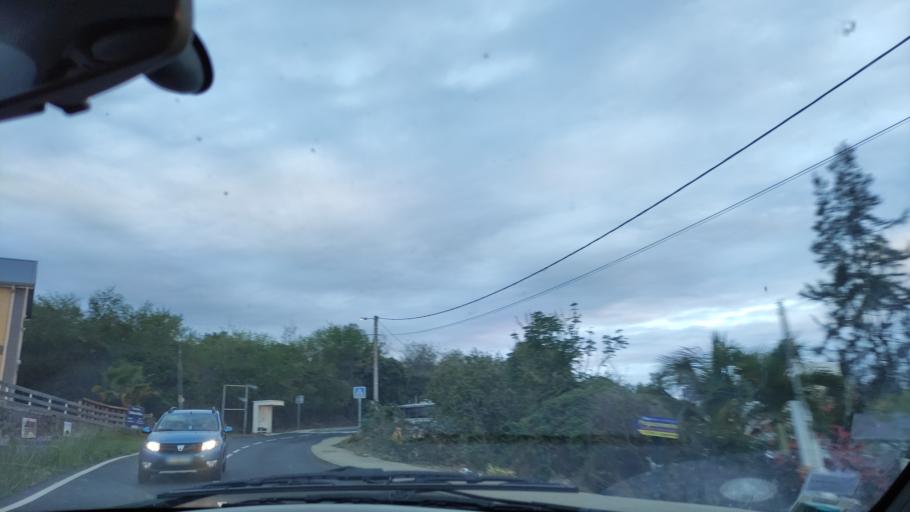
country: RE
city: Piton Saint-Leu
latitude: -21.2084
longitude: 55.2974
